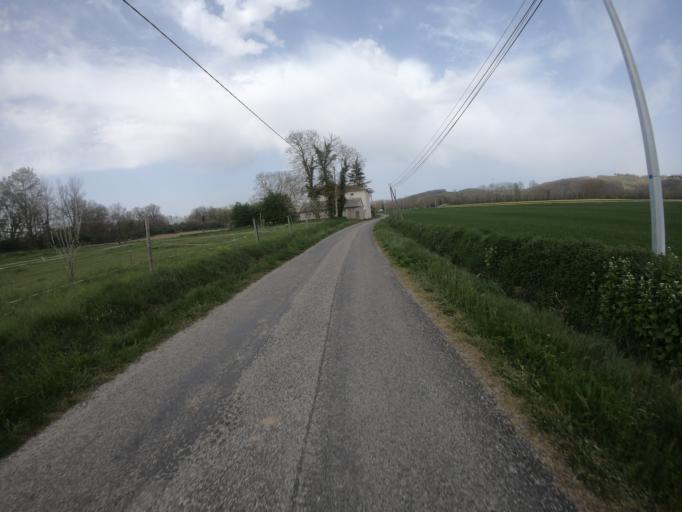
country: FR
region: Languedoc-Roussillon
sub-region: Departement de l'Aude
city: Belpech
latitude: 43.1700
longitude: 1.7260
